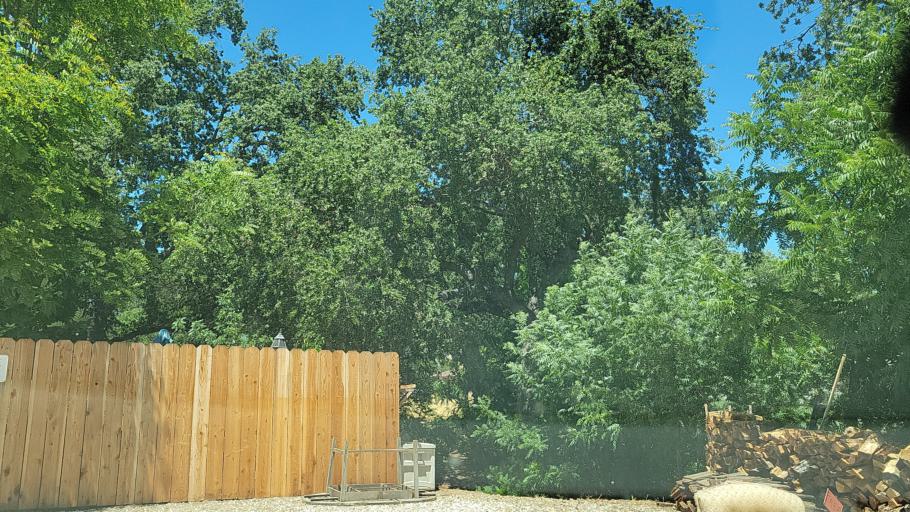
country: US
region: California
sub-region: San Luis Obispo County
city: Atascadero
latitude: 35.4807
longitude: -120.6630
